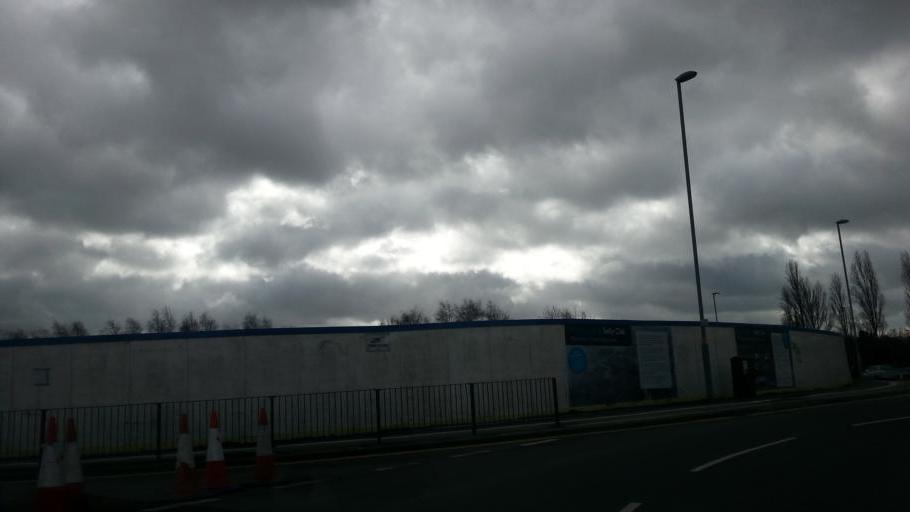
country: GB
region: England
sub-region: City and Borough of Birmingham
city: Bartley Green
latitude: 52.4440
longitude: -1.9419
